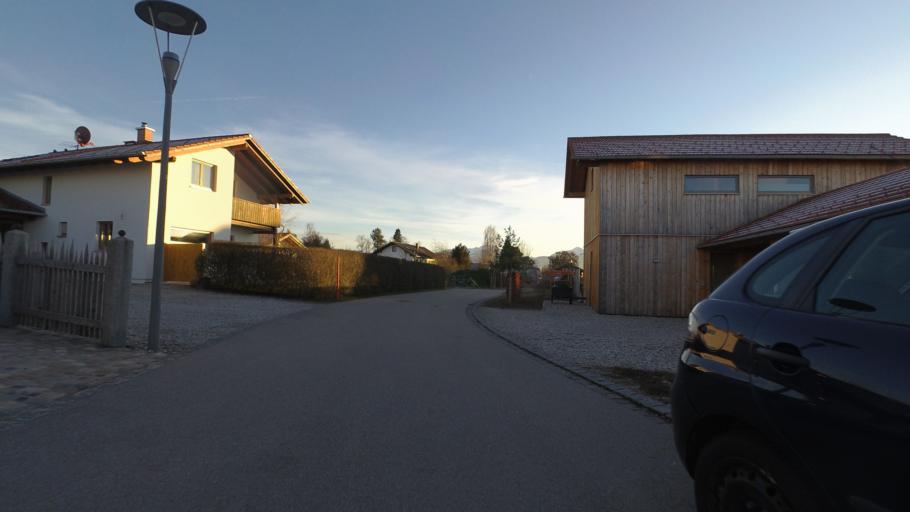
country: DE
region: Bavaria
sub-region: Upper Bavaria
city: Chieming
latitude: 47.8982
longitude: 12.5357
